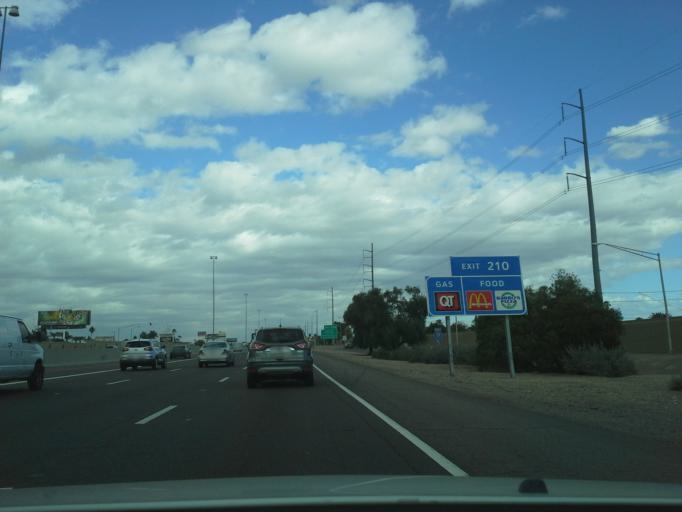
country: US
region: Arizona
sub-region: Maricopa County
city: Glendale
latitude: 33.5976
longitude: -112.1167
